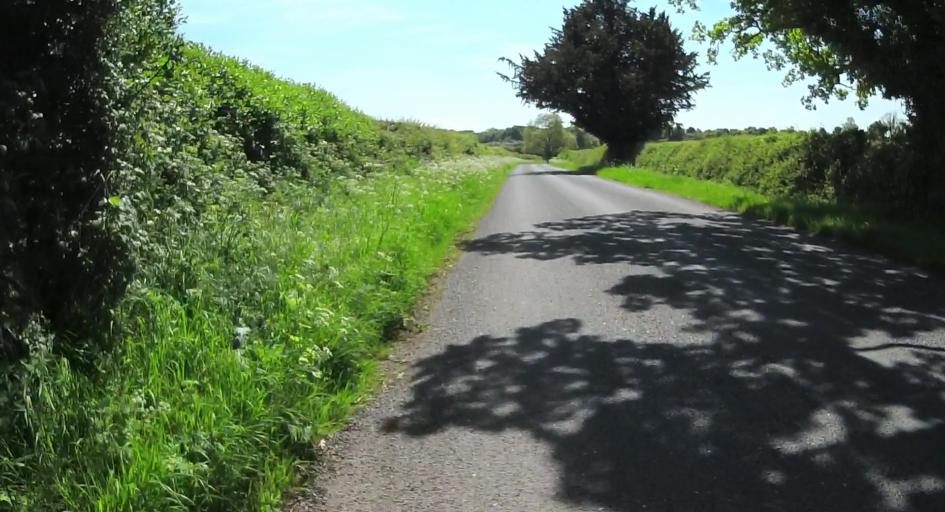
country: GB
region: England
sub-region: Hampshire
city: Four Marks
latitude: 51.1487
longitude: -1.1473
